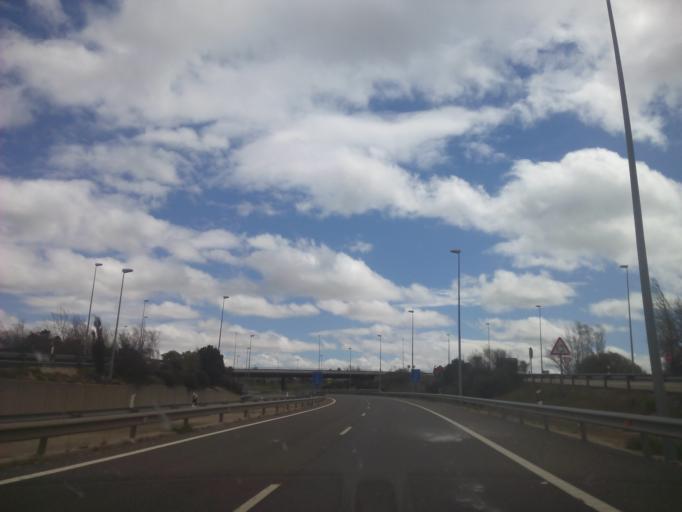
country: ES
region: Castille and Leon
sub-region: Provincia de Salamanca
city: Carbajosa de la Sagrada
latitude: 40.9451
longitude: -5.6439
